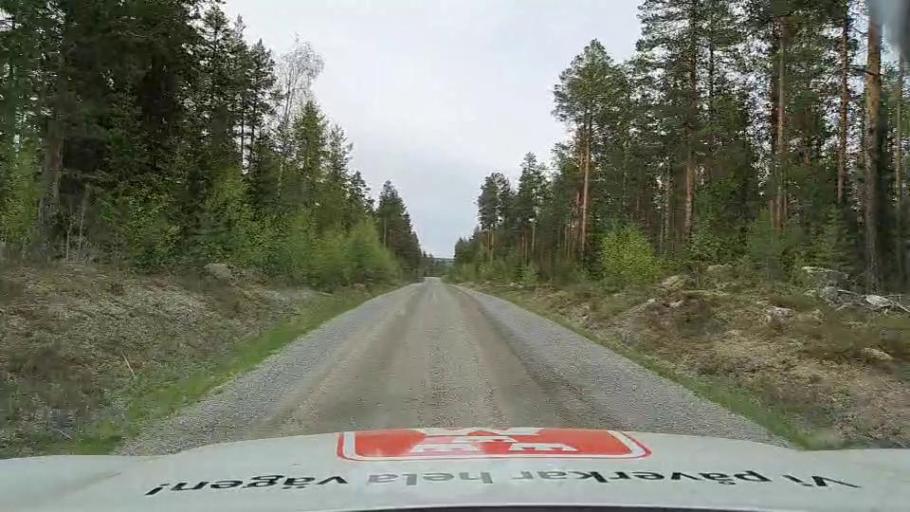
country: SE
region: Jaemtland
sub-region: Braecke Kommun
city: Braecke
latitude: 62.4776
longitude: 14.9169
